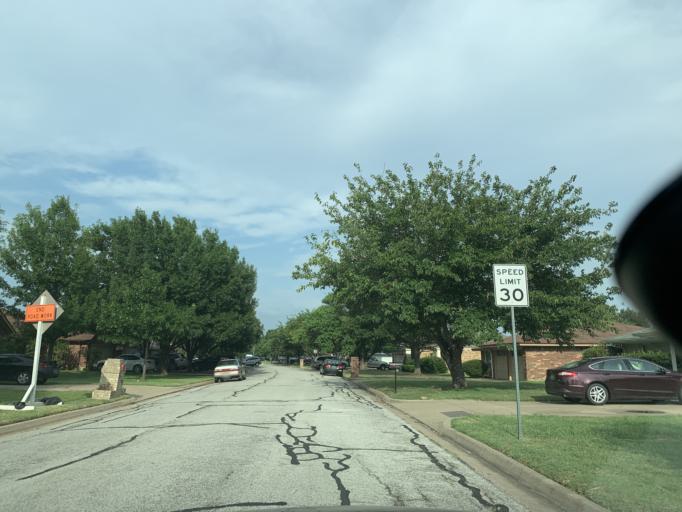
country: US
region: Texas
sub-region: Tarrant County
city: Watauga
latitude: 32.8781
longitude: -97.2374
